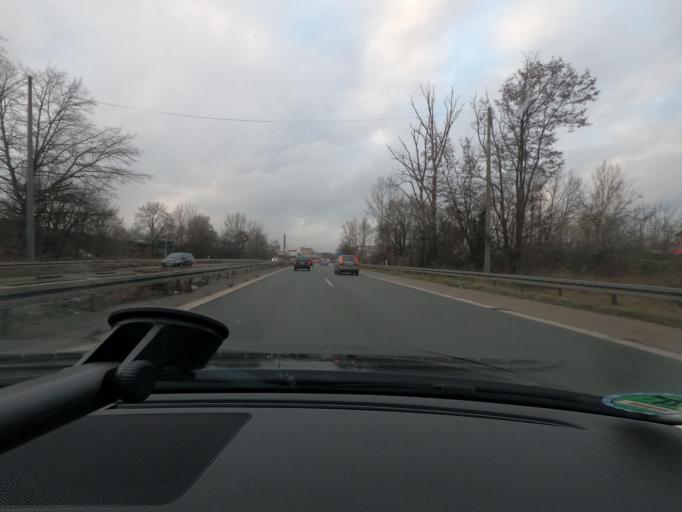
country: DE
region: Bavaria
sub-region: Regierungsbezirk Mittelfranken
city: Wetzendorf
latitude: 49.4587
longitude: 11.0204
